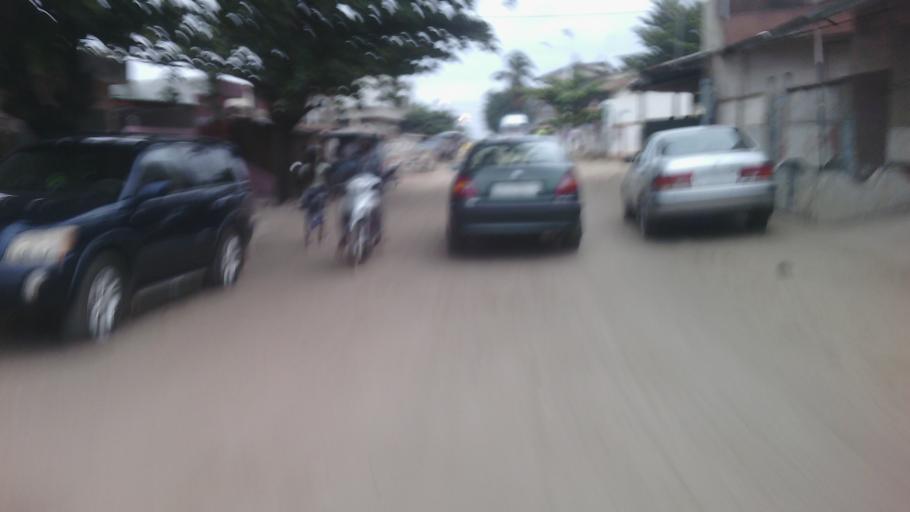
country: BJ
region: Atlantique
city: Abomey-Calavi
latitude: 6.3928
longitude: 2.3676
